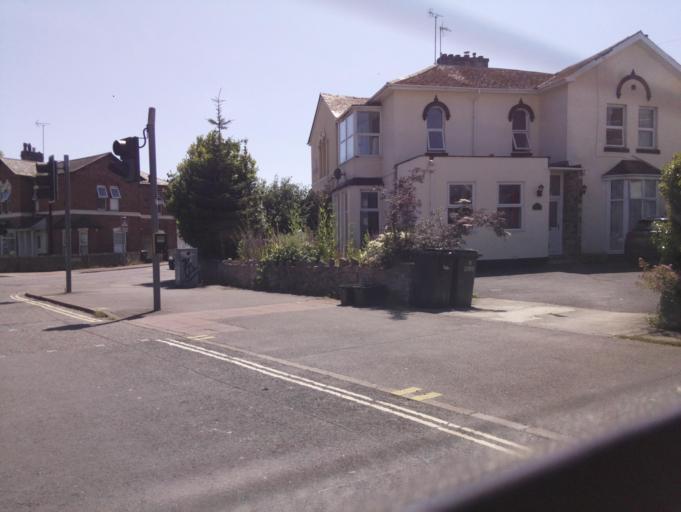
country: GB
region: England
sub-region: Borough of Torbay
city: Torquay
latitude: 50.4682
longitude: -3.5439
